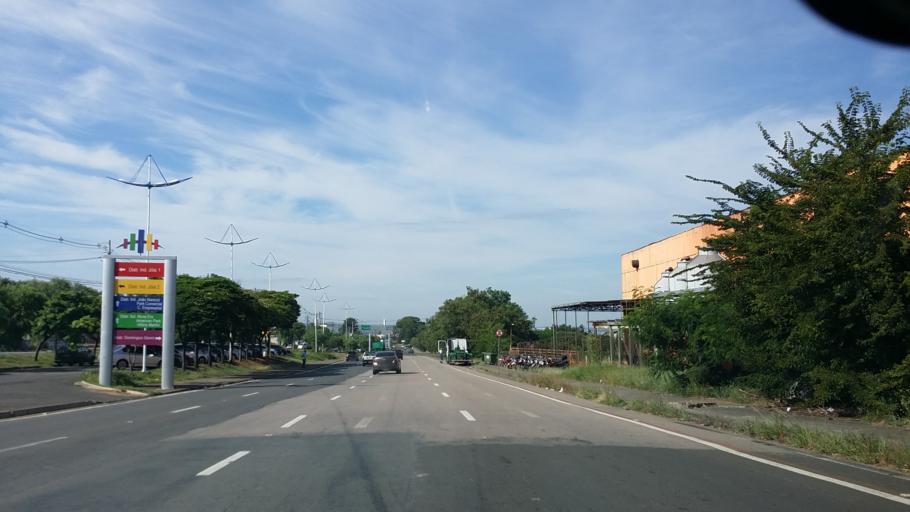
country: BR
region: Sao Paulo
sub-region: Indaiatuba
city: Indaiatuba
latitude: -23.1259
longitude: -47.2262
